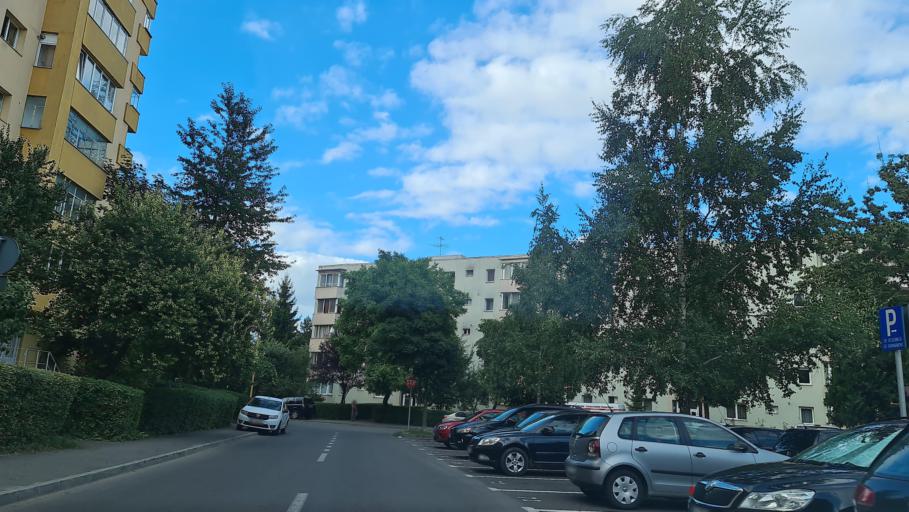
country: RO
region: Brasov
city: Brasov
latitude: 45.6451
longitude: 25.6191
